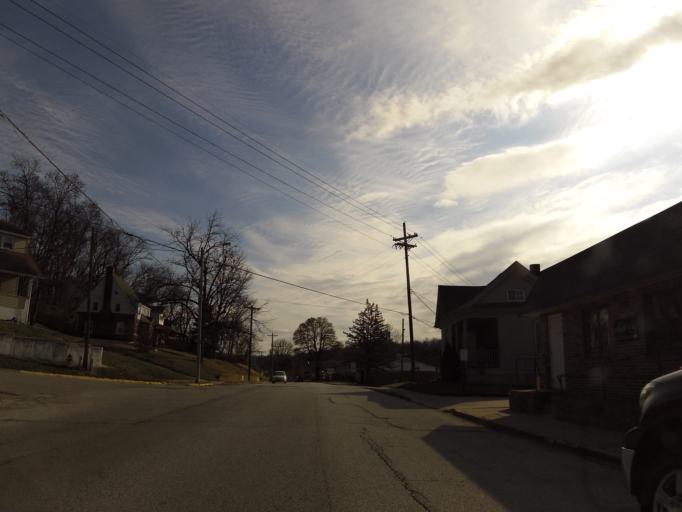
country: US
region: Missouri
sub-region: Marion County
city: Hannibal
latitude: 39.7053
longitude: -91.3857
